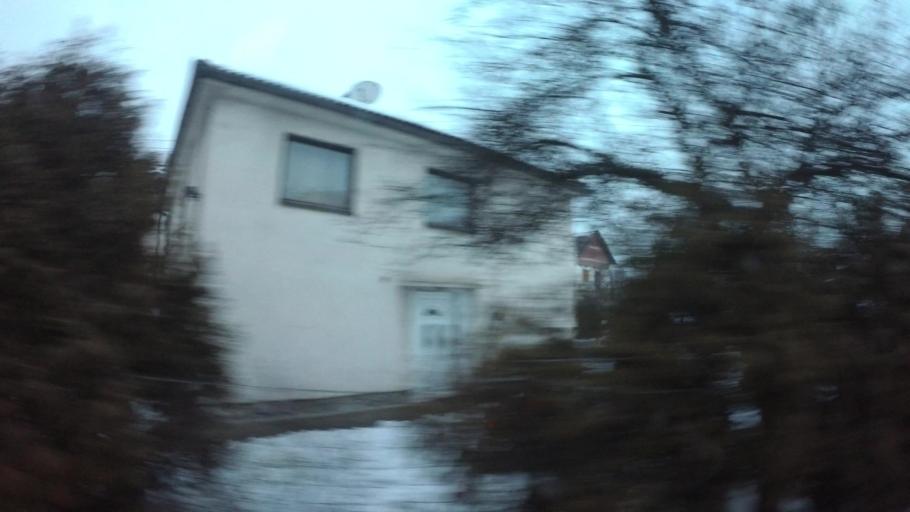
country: BA
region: Federation of Bosnia and Herzegovina
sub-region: Kanton Sarajevo
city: Sarajevo
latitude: 43.8516
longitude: 18.3026
